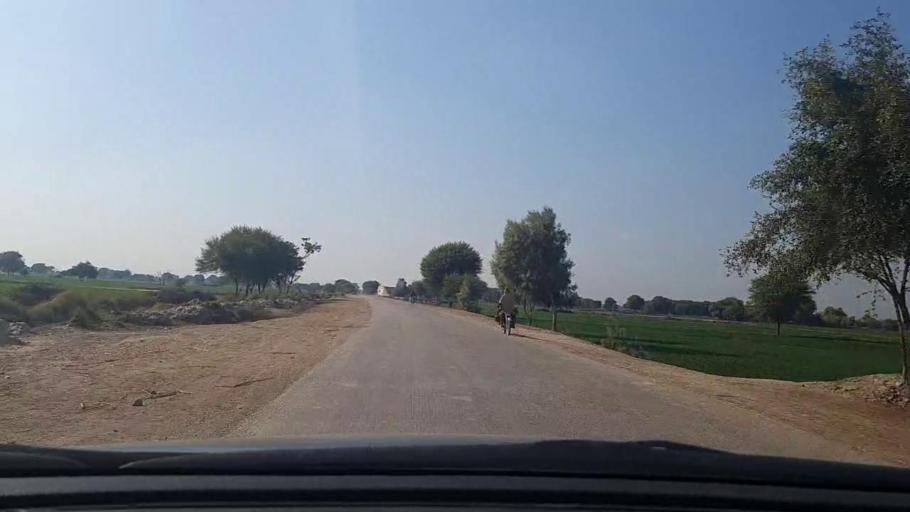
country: PK
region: Sindh
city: Daulatpur
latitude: 26.3150
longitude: 68.0672
